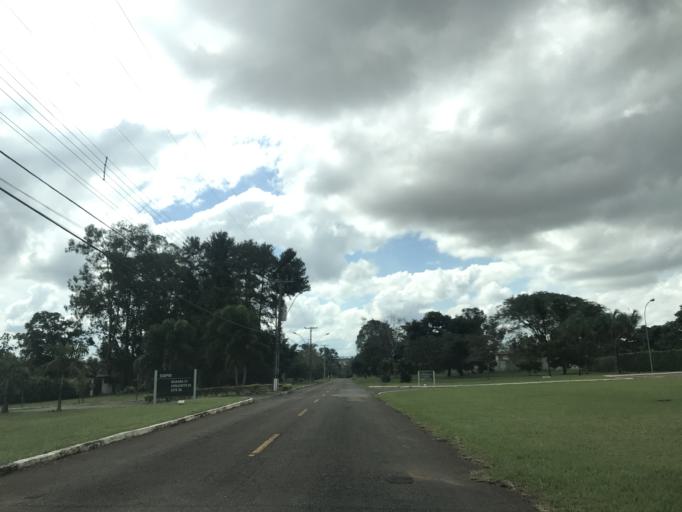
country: BR
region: Federal District
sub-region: Brasilia
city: Brasilia
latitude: -15.8941
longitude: -47.9256
